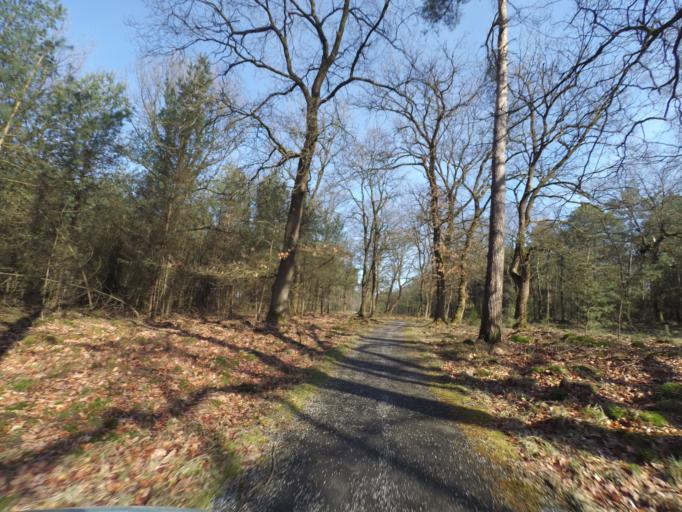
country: NL
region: Gelderland
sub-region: Gemeente Barneveld
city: Garderen
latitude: 52.1895
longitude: 5.7496
